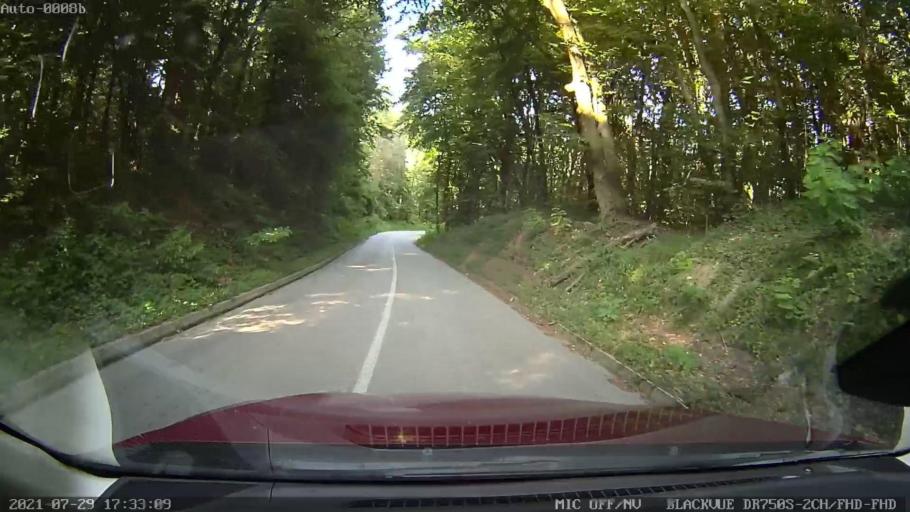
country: HR
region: Varazdinska
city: Vinica
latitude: 46.2958
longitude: 16.1367
